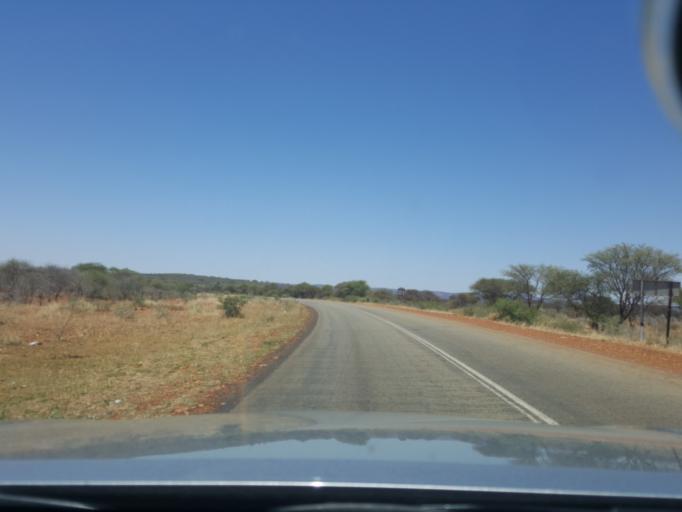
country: BW
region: South East
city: Otse
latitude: -25.1181
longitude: 25.9453
